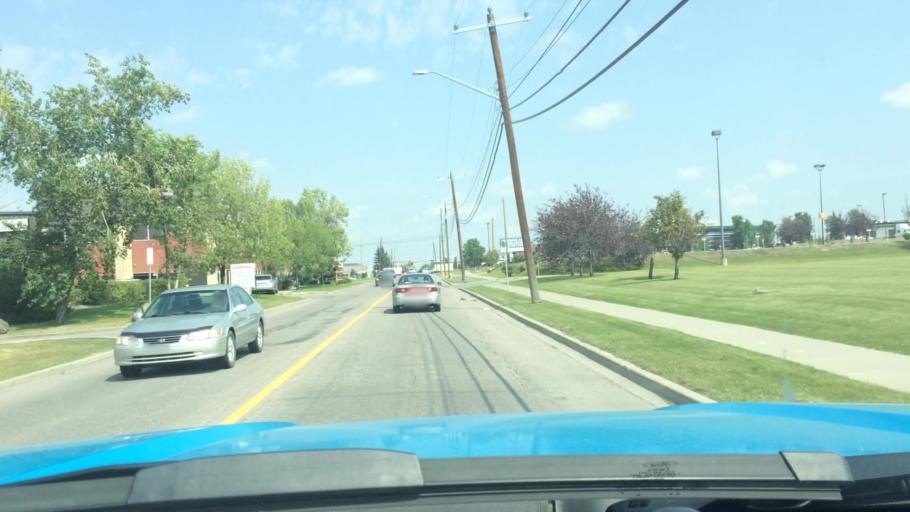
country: CA
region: Alberta
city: Calgary
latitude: 51.0784
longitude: -114.0051
